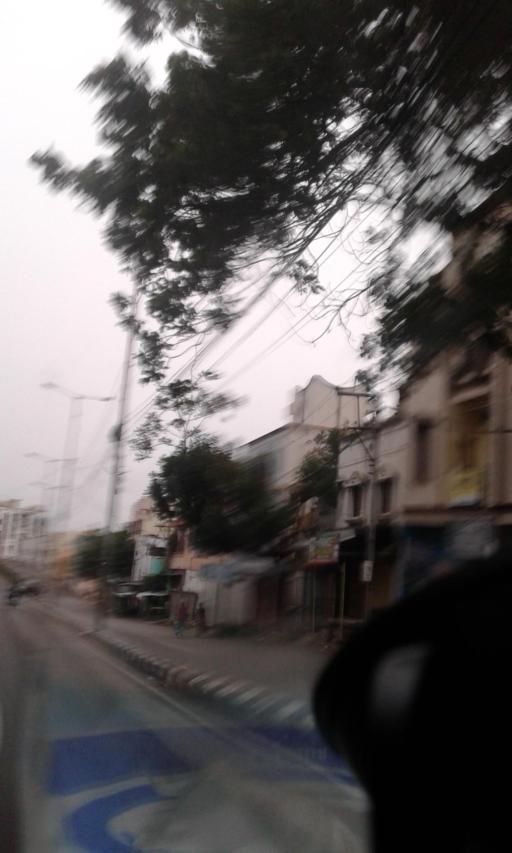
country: IN
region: Telangana
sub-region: Rangareddi
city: Gaddi Annaram
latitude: 17.3669
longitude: 78.4934
